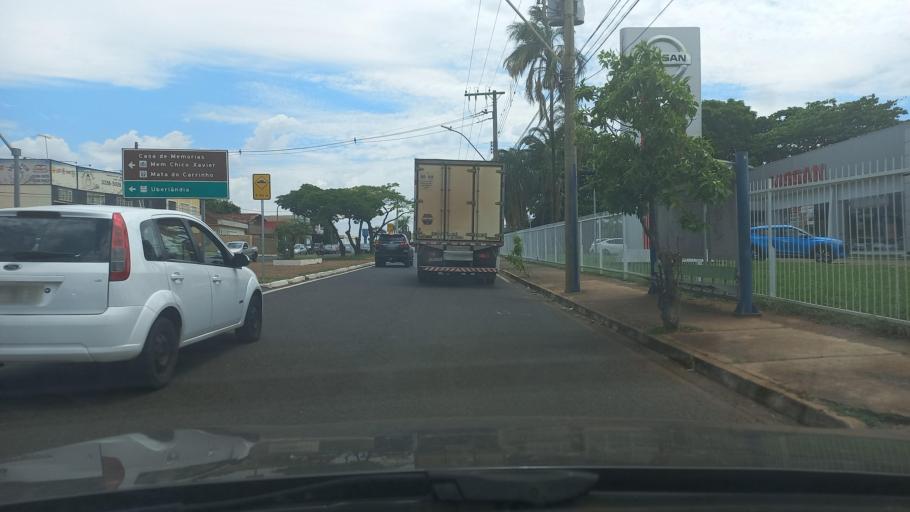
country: BR
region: Minas Gerais
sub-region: Uberaba
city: Uberaba
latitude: -19.7704
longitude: -47.9573
